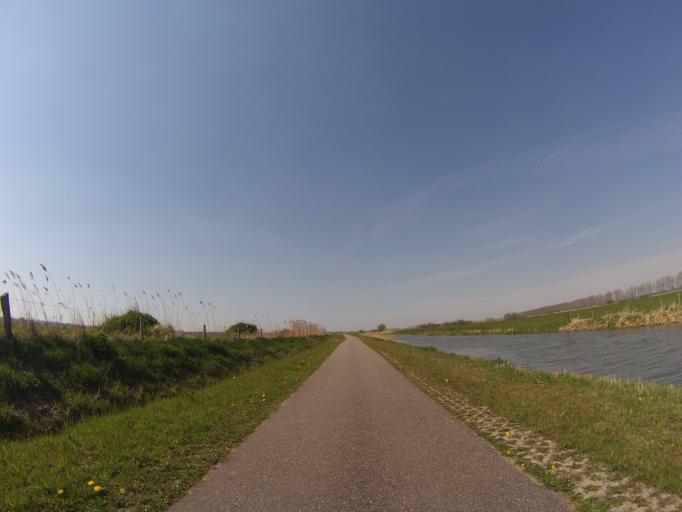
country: NL
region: Gelderland
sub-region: Gemeente Wageningen
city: Wageningen
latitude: 51.9742
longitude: 5.6253
